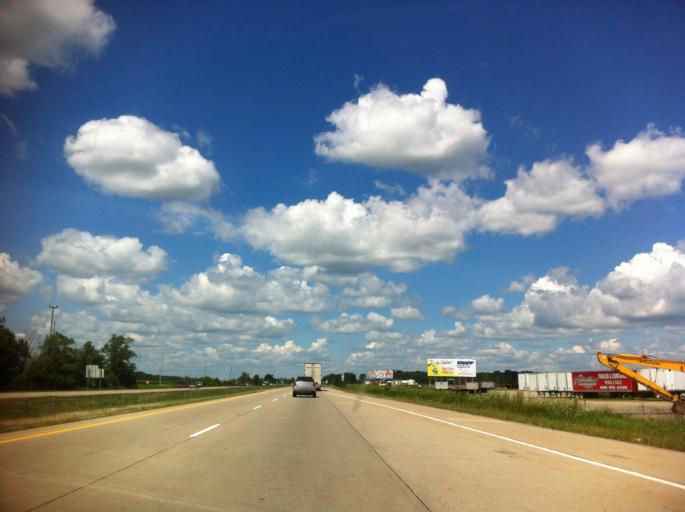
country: US
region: Ohio
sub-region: Lucas County
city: Sylvania
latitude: 41.7515
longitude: -83.6940
